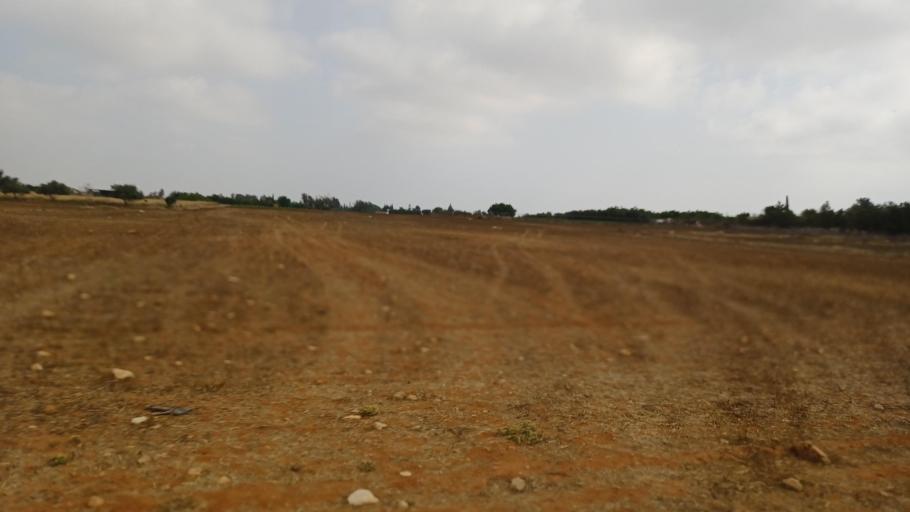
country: CY
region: Ammochostos
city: Deryneia
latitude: 35.0605
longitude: 33.9381
